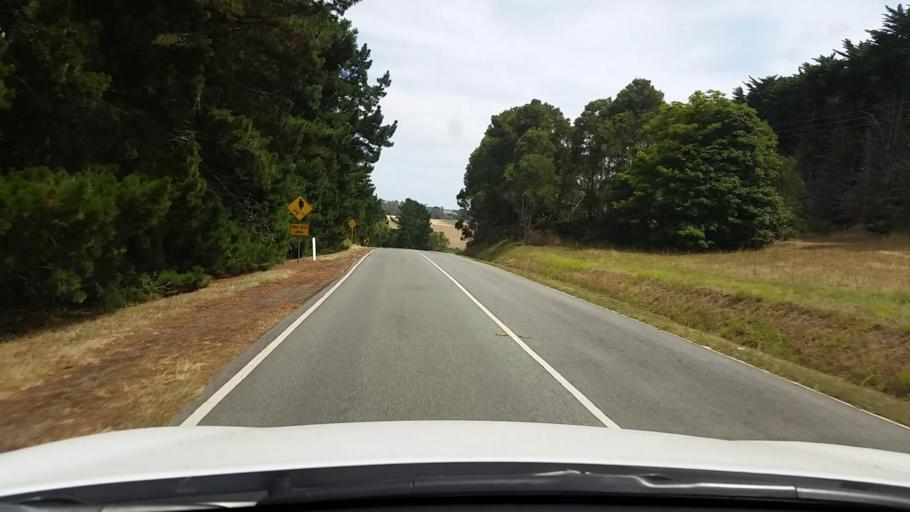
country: AU
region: Victoria
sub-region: Mornington Peninsula
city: McCrae
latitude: -38.4804
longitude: 144.9559
